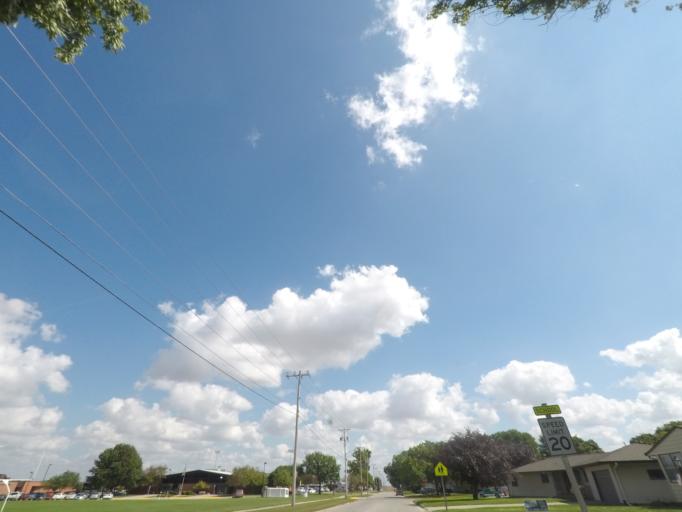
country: US
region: Iowa
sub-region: Story County
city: Nevada
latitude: 42.0191
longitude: -93.4411
